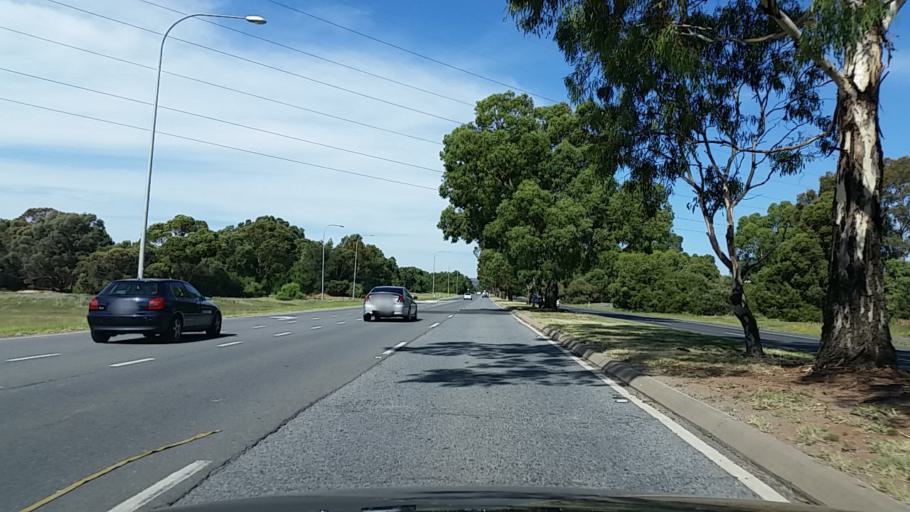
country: AU
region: South Australia
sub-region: Port Adelaide Enfield
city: Enfield
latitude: -34.8263
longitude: 138.6046
